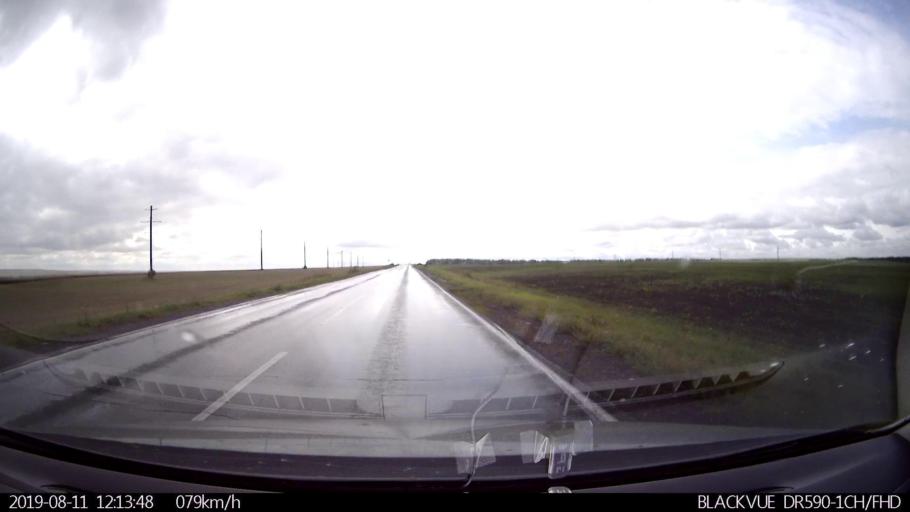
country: RU
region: Ulyanovsk
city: Ignatovka
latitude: 53.9584
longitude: 47.9885
